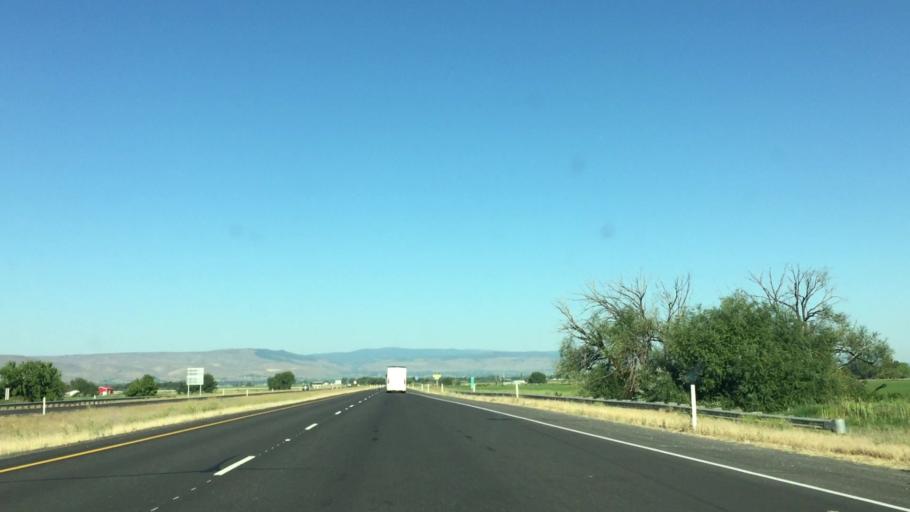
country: US
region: Washington
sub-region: Kittitas County
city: Kittitas
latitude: 46.9720
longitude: -120.4218
